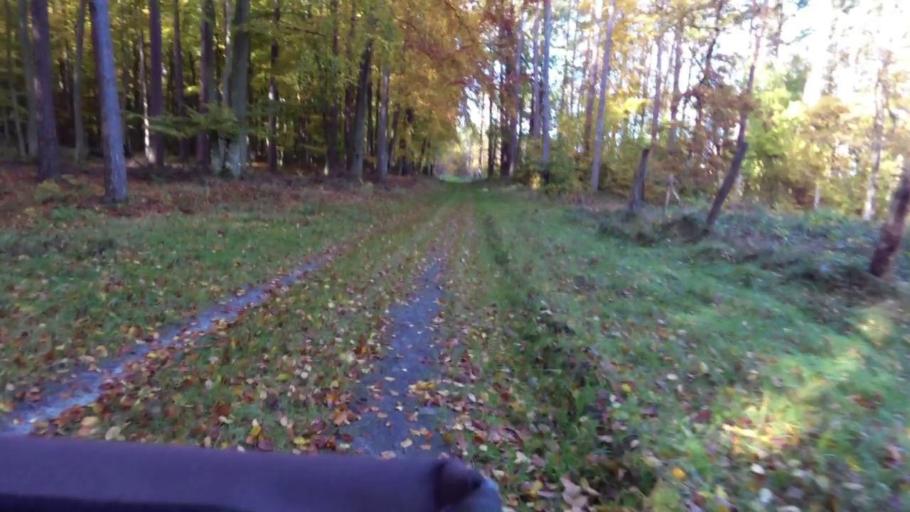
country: PL
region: West Pomeranian Voivodeship
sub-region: Powiat kamienski
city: Miedzyzdroje
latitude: 53.8634
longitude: 14.5207
